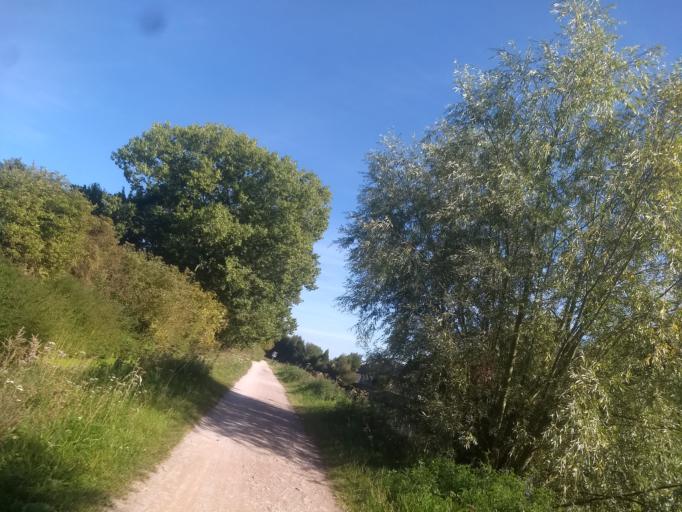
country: FR
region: Nord-Pas-de-Calais
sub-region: Departement du Pas-de-Calais
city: Feuchy
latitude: 50.3003
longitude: 2.8265
